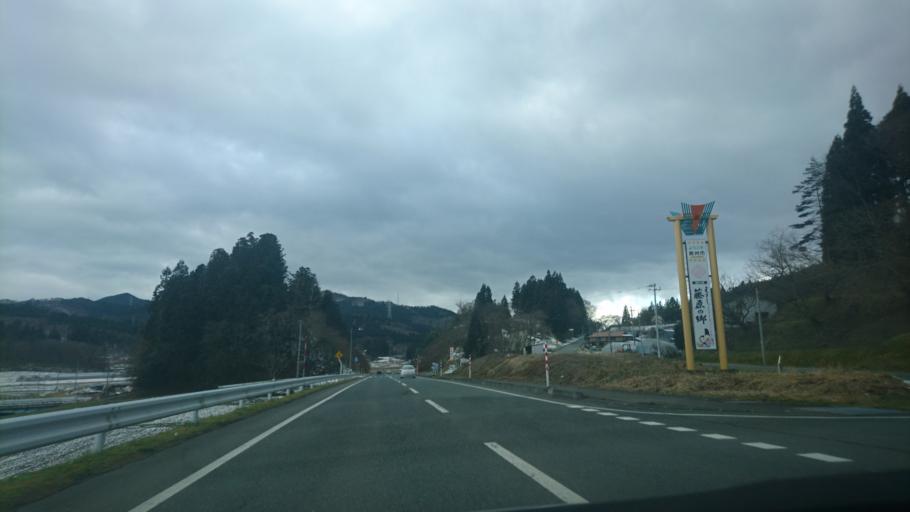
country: JP
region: Iwate
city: Mizusawa
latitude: 39.1809
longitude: 141.2898
